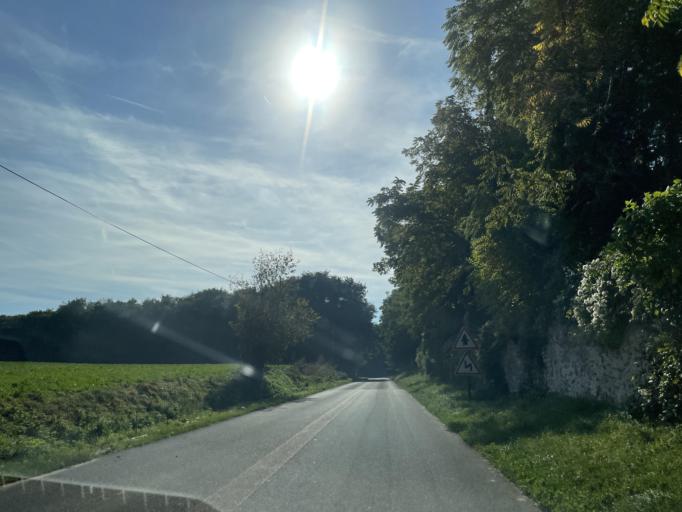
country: FR
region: Ile-de-France
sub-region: Departement de Seine-et-Marne
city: Saint-Jean-les-Deux-Jumeaux
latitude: 48.9385
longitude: 2.9862
